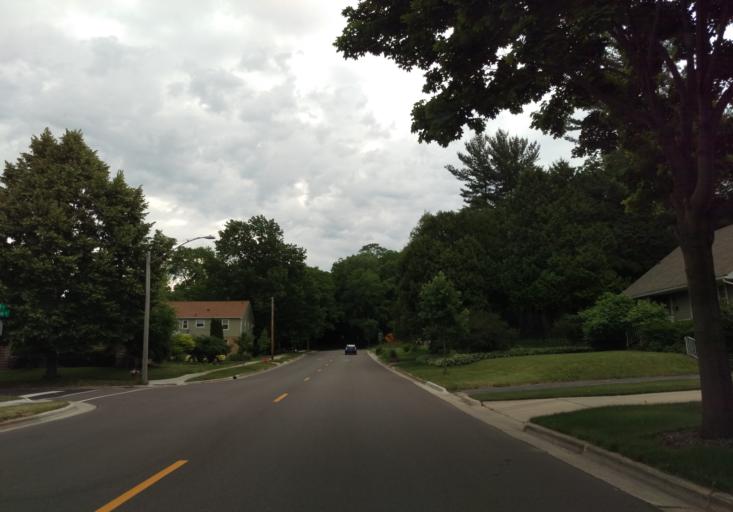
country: US
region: Wisconsin
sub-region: Dane County
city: Shorewood Hills
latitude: 43.0694
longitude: -89.4457
